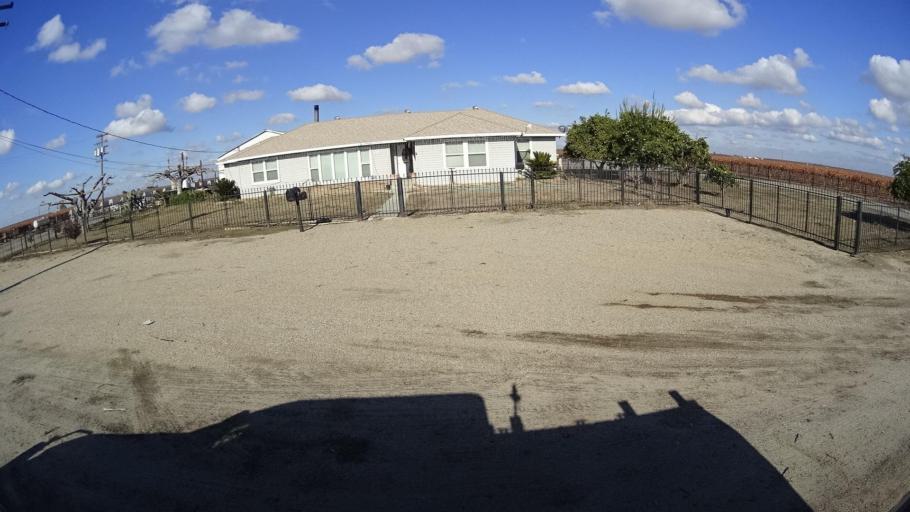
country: US
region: California
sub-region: Kern County
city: Delano
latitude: 35.7322
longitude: -119.3327
